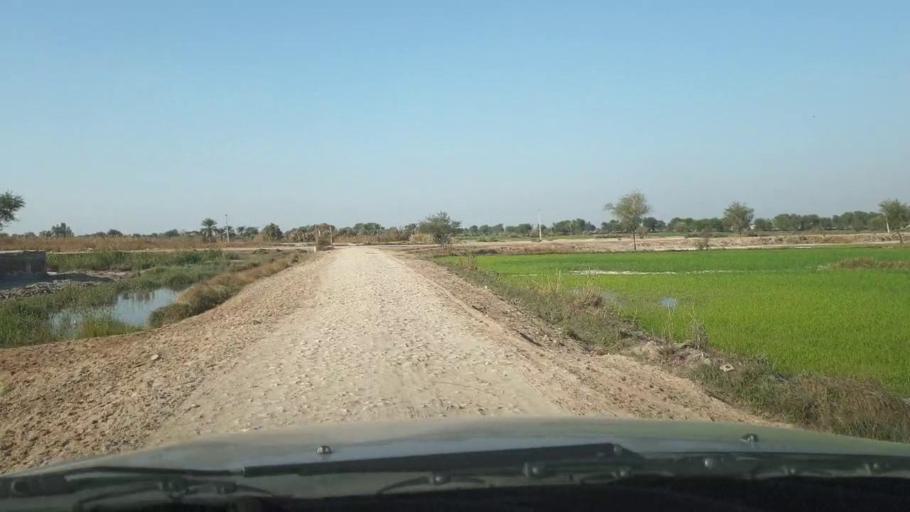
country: PK
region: Sindh
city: Mirpur Mathelo
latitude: 27.9827
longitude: 69.5355
